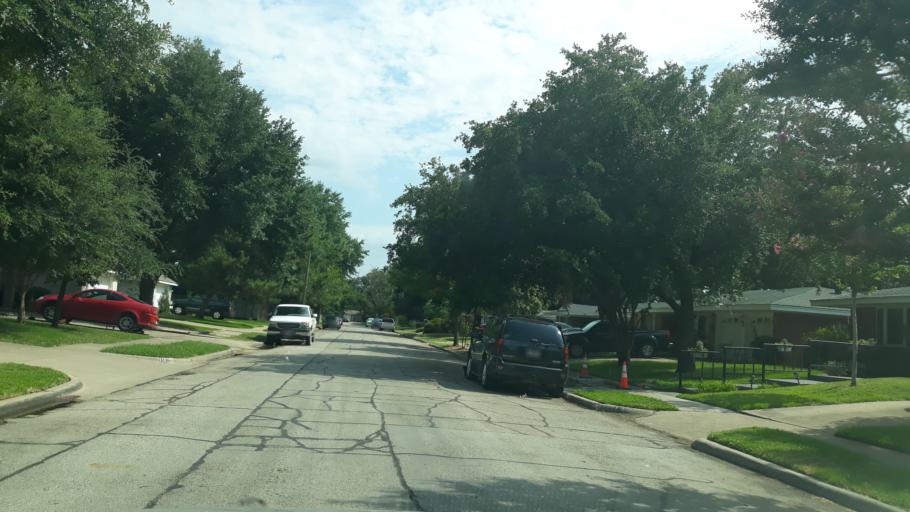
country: US
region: Texas
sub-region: Dallas County
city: Irving
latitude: 32.8146
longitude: -96.9799
